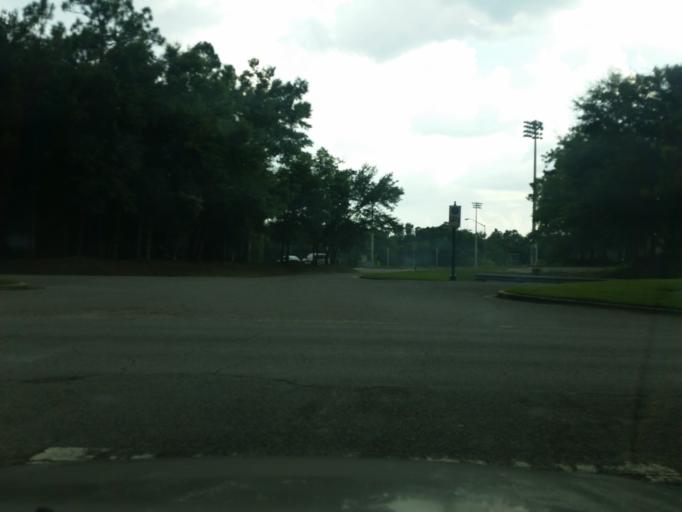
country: US
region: Florida
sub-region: Escambia County
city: Ferry Pass
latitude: 30.5416
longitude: -87.2017
